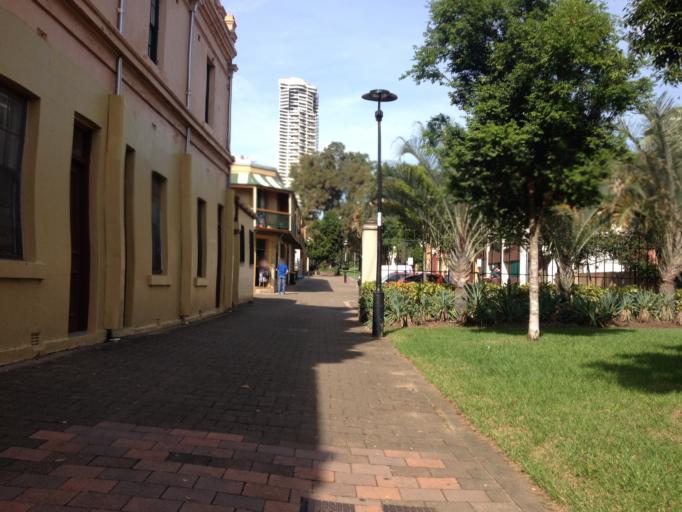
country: AU
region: New South Wales
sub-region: City of Sydney
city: Darlinghurst
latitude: -33.8710
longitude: 151.2201
